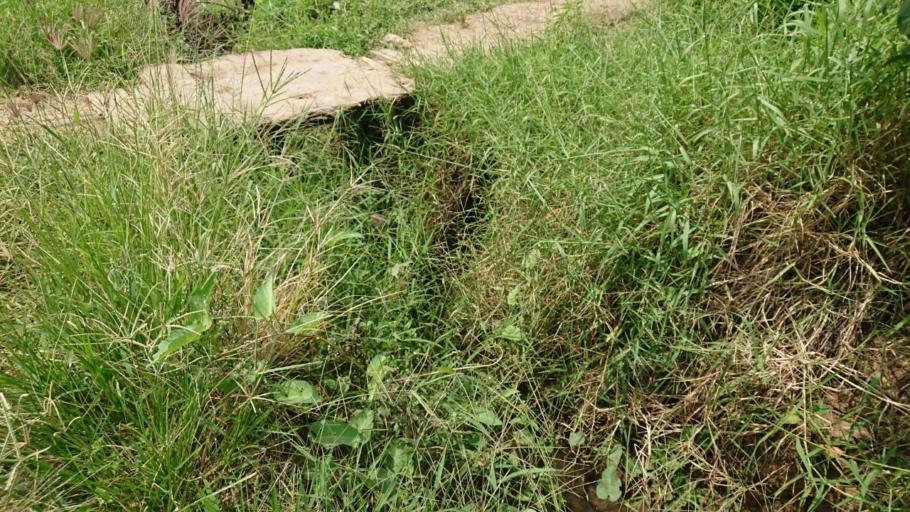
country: ID
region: West Java
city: Bekasi
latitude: -6.1305
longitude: 106.9629
